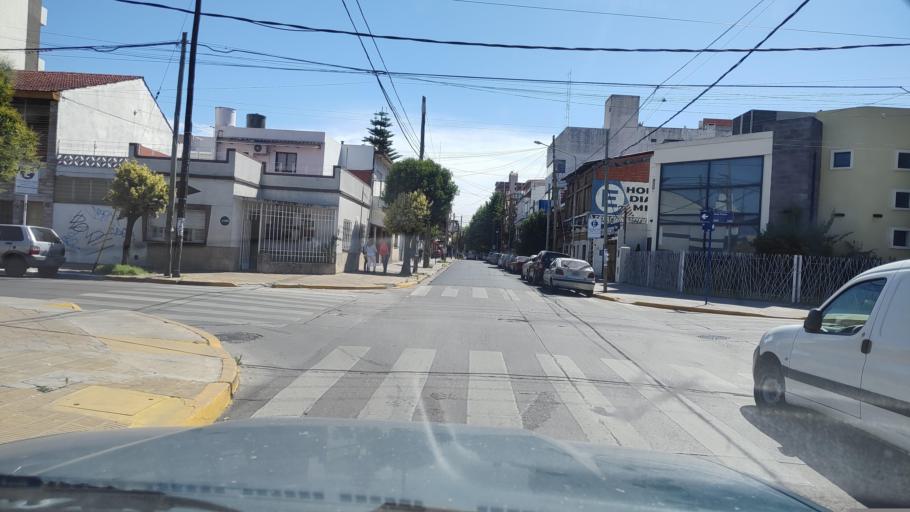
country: AR
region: Buenos Aires
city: San Justo
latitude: -34.6806
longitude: -58.5613
